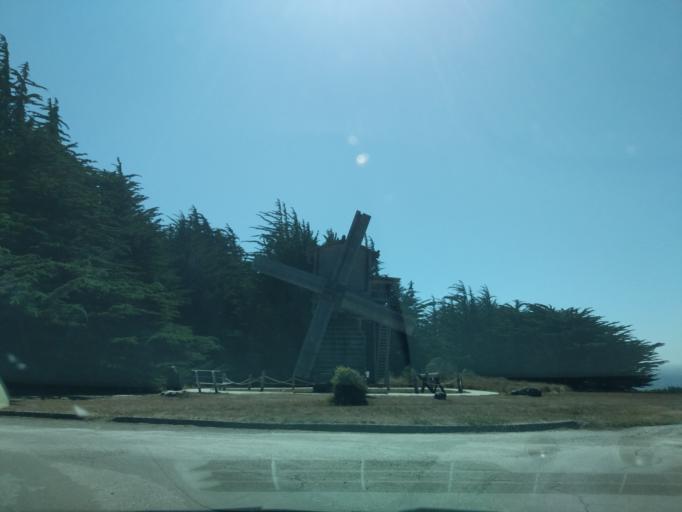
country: US
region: California
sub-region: Sonoma County
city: Monte Rio
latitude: 38.5153
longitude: -123.2475
